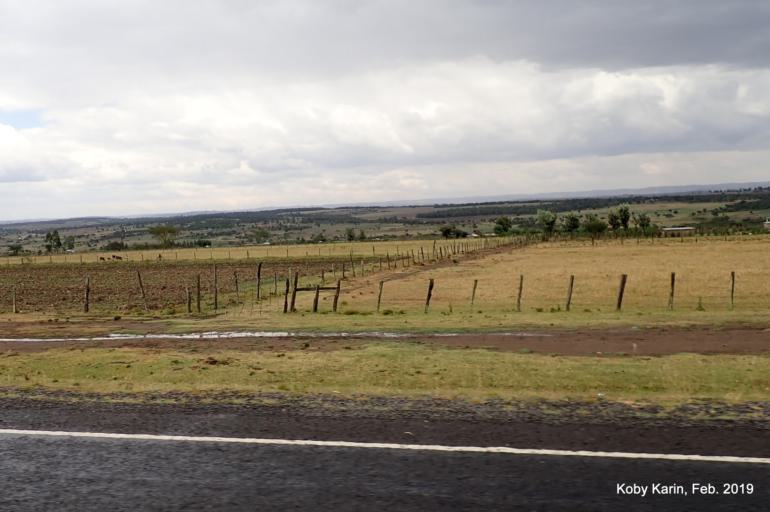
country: KE
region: Narok
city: Narok
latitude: -0.9996
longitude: 35.6018
